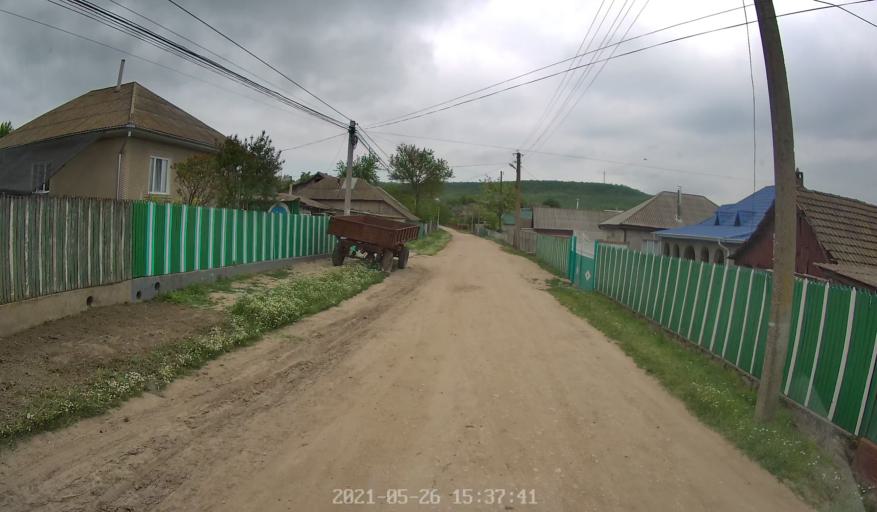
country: MD
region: Hincesti
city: Dancu
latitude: 46.6696
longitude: 28.3184
